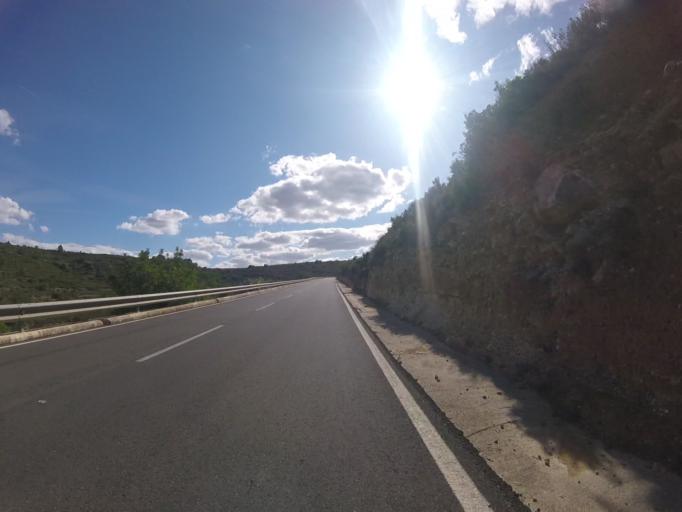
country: ES
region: Valencia
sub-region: Provincia de Castello
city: Cuevas de Vinroma
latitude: 40.3172
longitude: 0.1343
